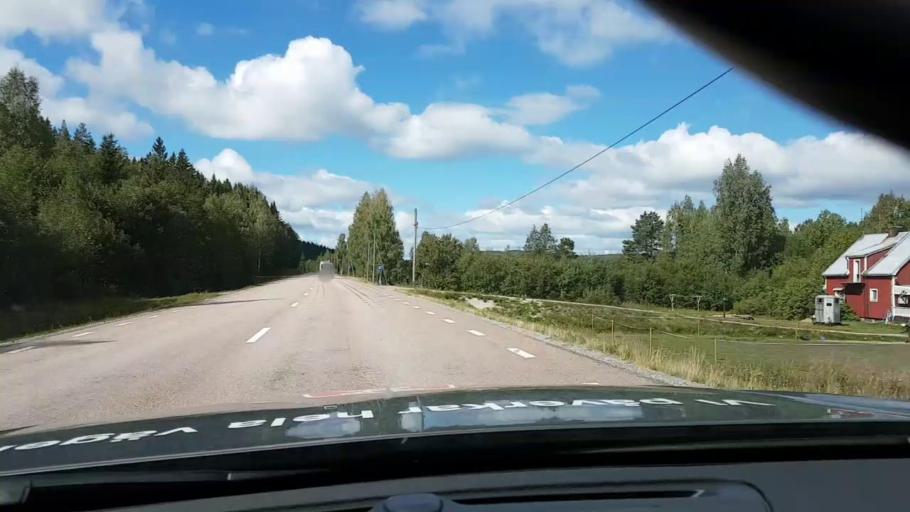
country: SE
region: Vaesternorrland
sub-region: OErnskoeldsviks Kommun
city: Bjasta
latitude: 63.3573
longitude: 18.4801
